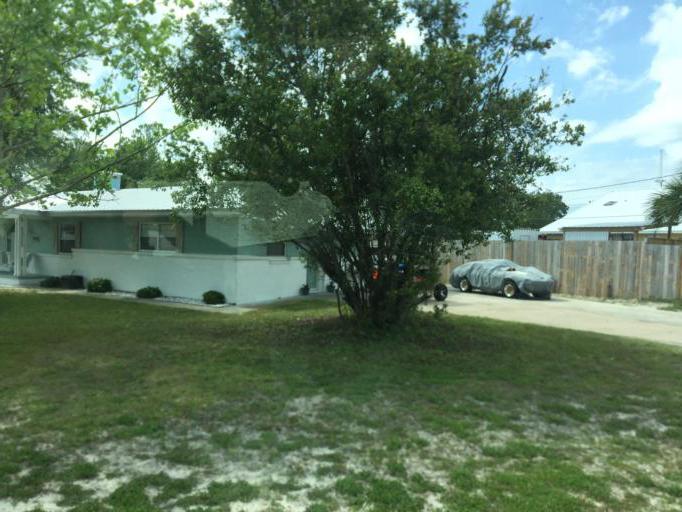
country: US
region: Florida
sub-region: Bay County
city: Laguna Beach
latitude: 30.2248
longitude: -85.8838
